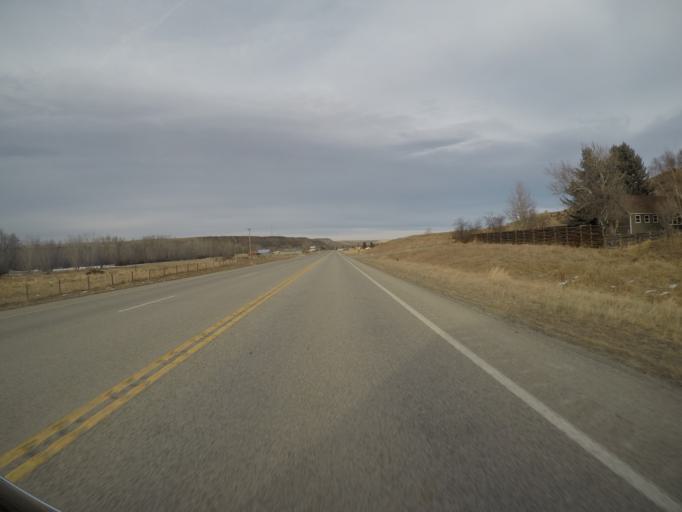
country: US
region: Montana
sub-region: Stillwater County
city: Absarokee
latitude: 45.5053
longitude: -109.4487
